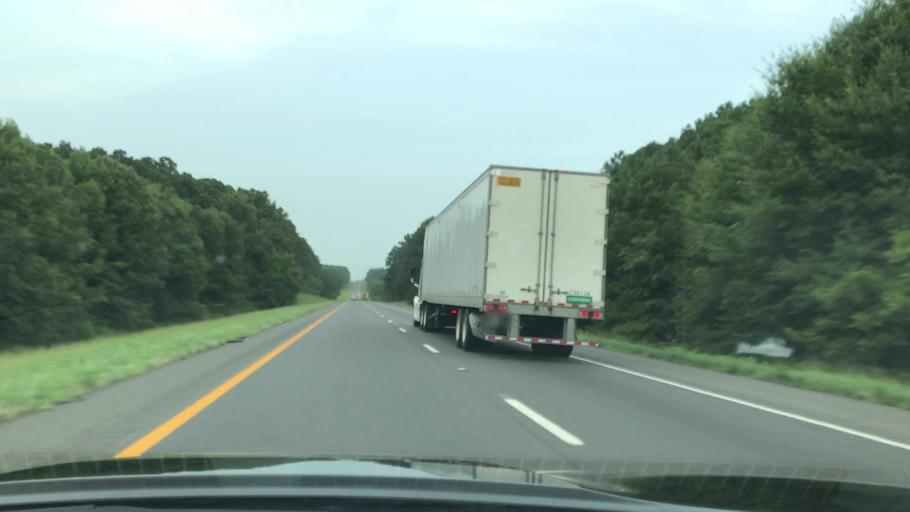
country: US
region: Texas
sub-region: Harrison County
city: Marshall
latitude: 32.4899
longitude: -94.3912
